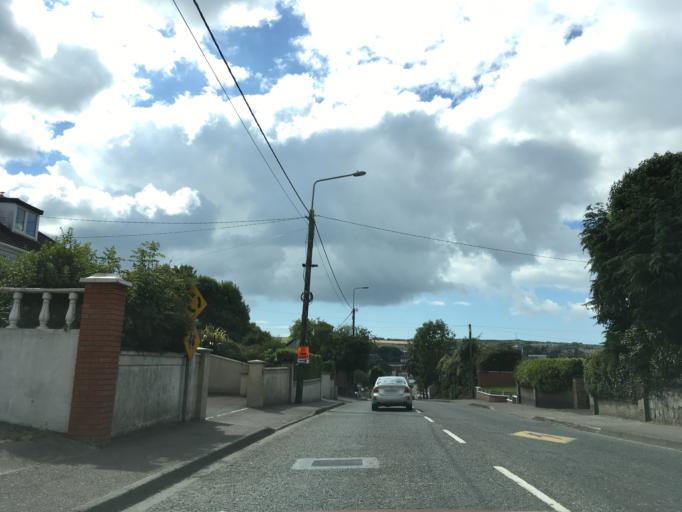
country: IE
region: Munster
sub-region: County Cork
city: Carrigaline
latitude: 51.8180
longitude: -8.3915
